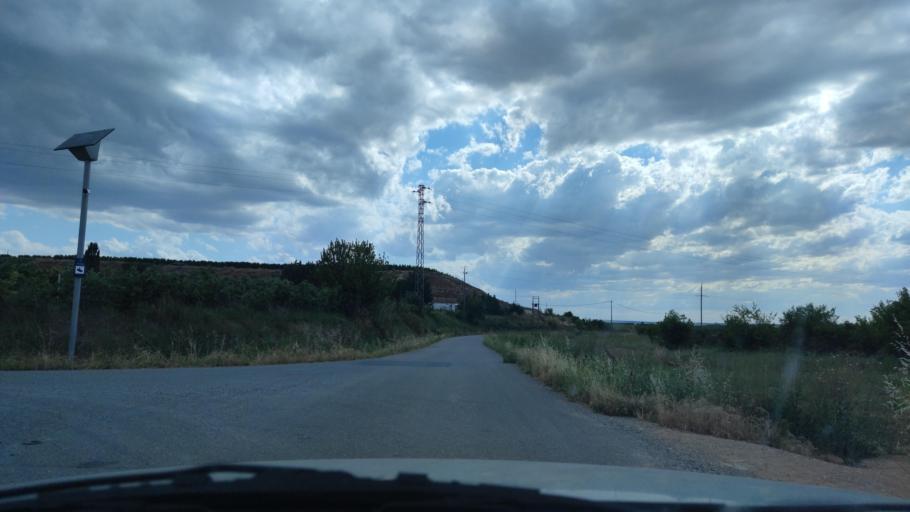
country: ES
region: Catalonia
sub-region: Provincia de Lleida
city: Lleida
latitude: 41.5961
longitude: 0.5757
